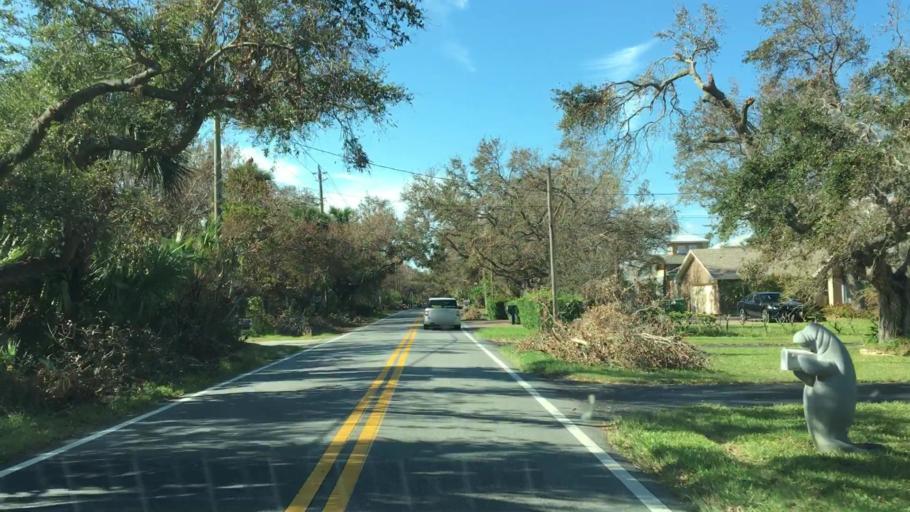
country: US
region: Florida
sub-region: Brevard County
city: South Patrick Shores
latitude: 28.2137
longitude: -80.6413
